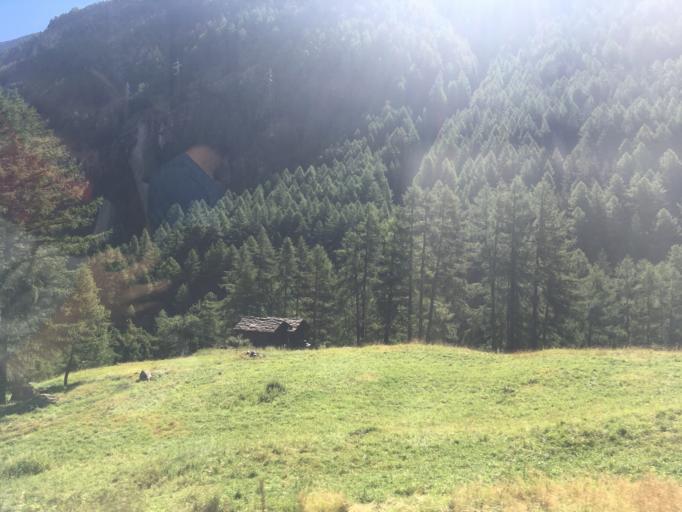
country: CH
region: Valais
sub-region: Visp District
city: Zermatt
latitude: 46.0374
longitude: 7.7608
